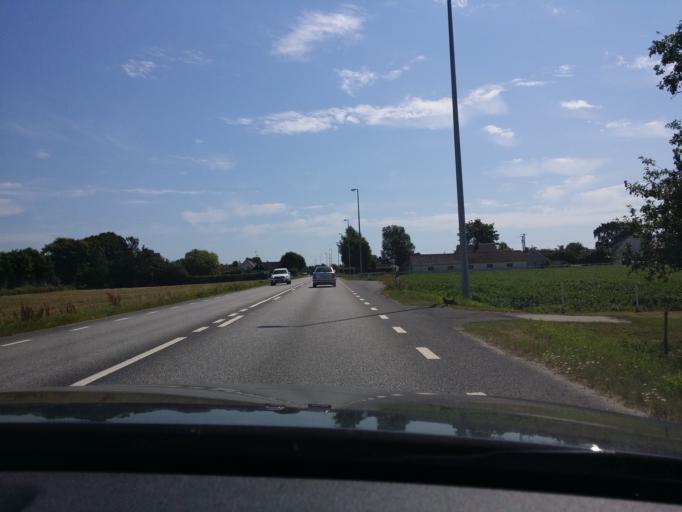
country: SE
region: Blekinge
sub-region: Solvesborgs Kommun
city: Soelvesborg
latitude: 56.0505
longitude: 14.6526
